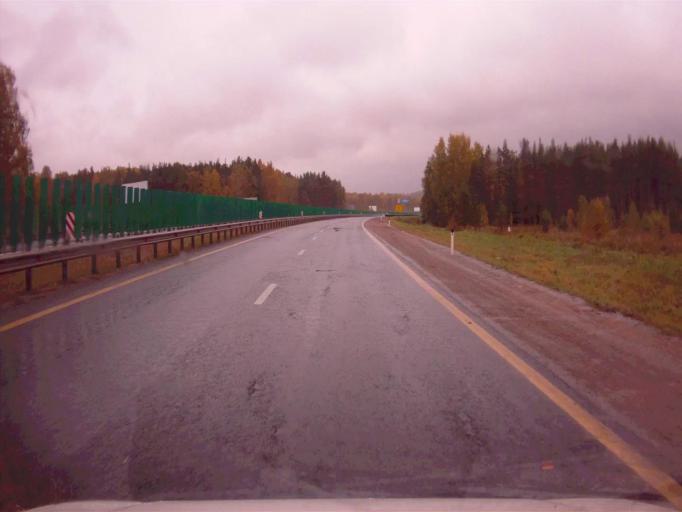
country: RU
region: Chelyabinsk
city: Dolgoderevenskoye
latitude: 55.3377
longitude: 61.3085
